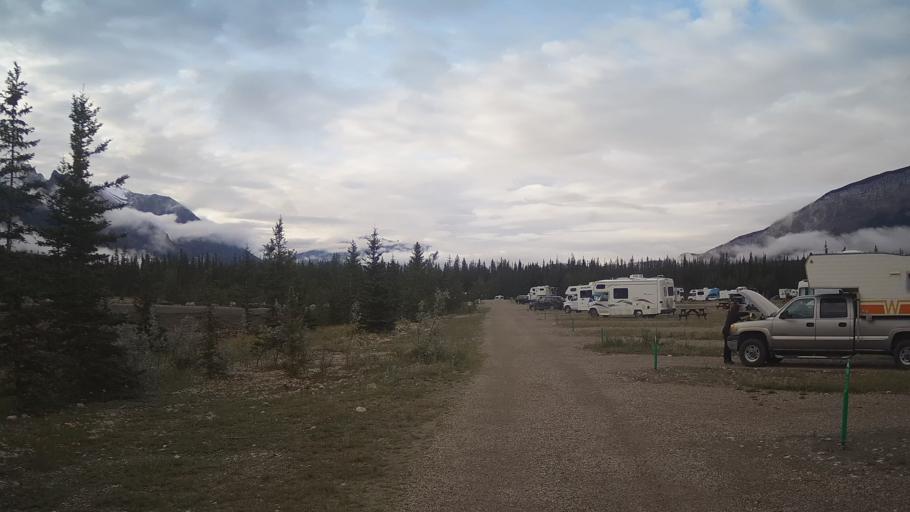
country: CA
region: Alberta
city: Jasper Park Lodge
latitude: 53.0182
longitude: -118.0848
